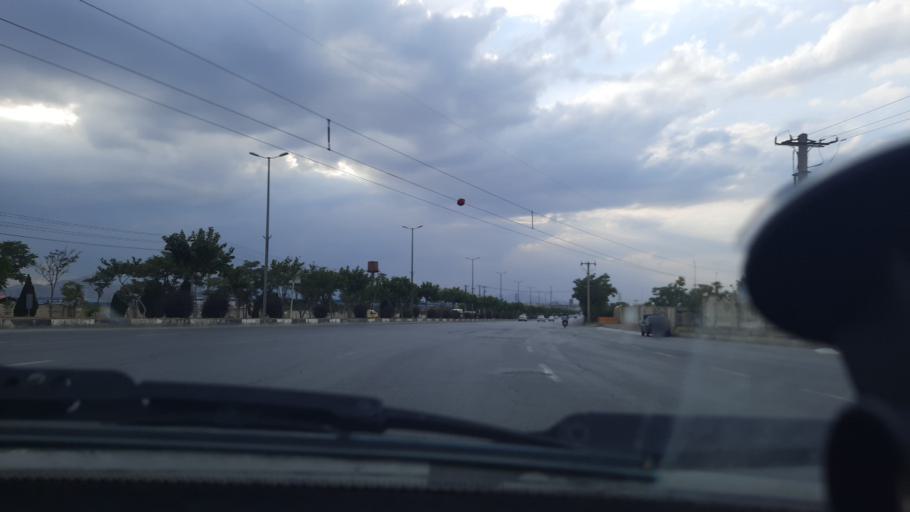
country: IR
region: Markazi
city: Arak
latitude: 34.0734
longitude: 49.7758
